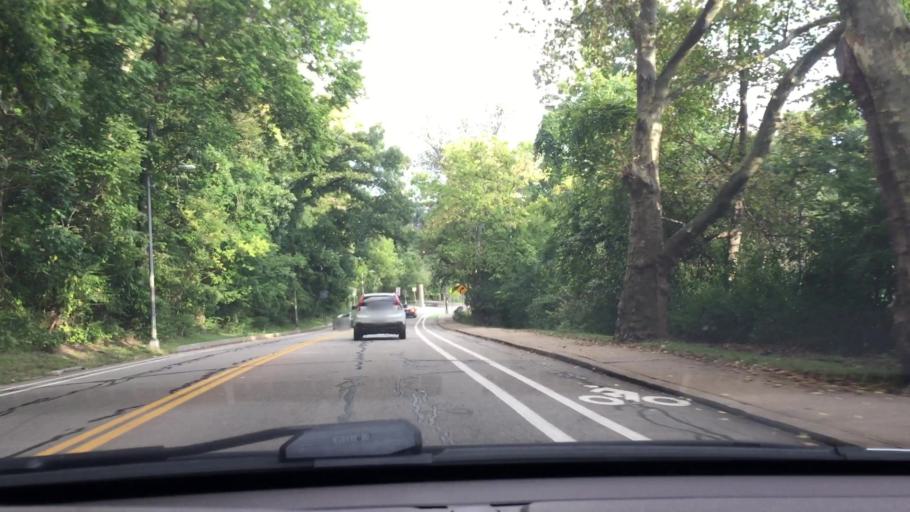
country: US
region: Pennsylvania
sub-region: Allegheny County
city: Bloomfield
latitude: 40.4301
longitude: -79.9387
